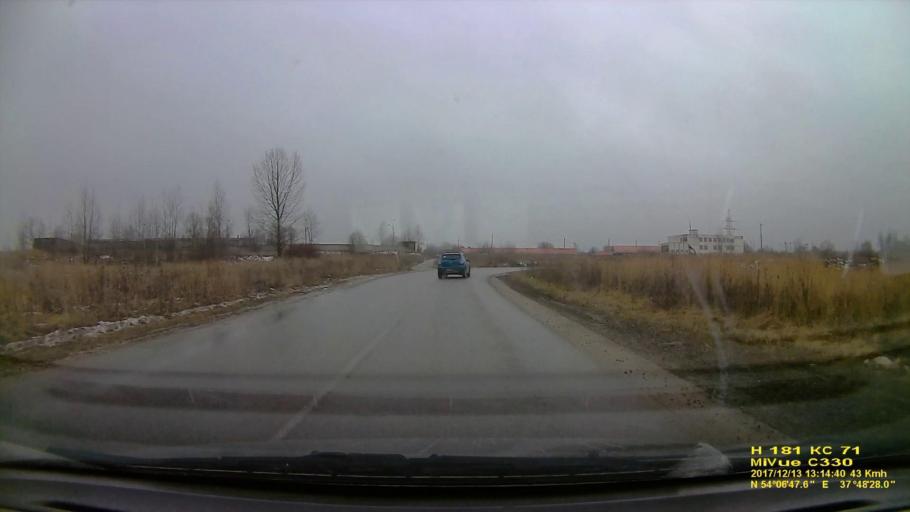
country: RU
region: Tula
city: Bolokhovo
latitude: 54.1129
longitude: 37.8080
